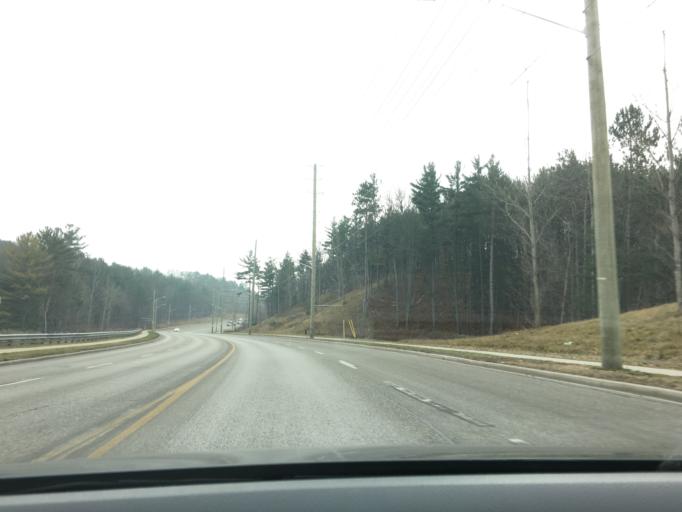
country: CA
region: Ontario
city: Barrie
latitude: 44.3895
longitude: -79.7324
